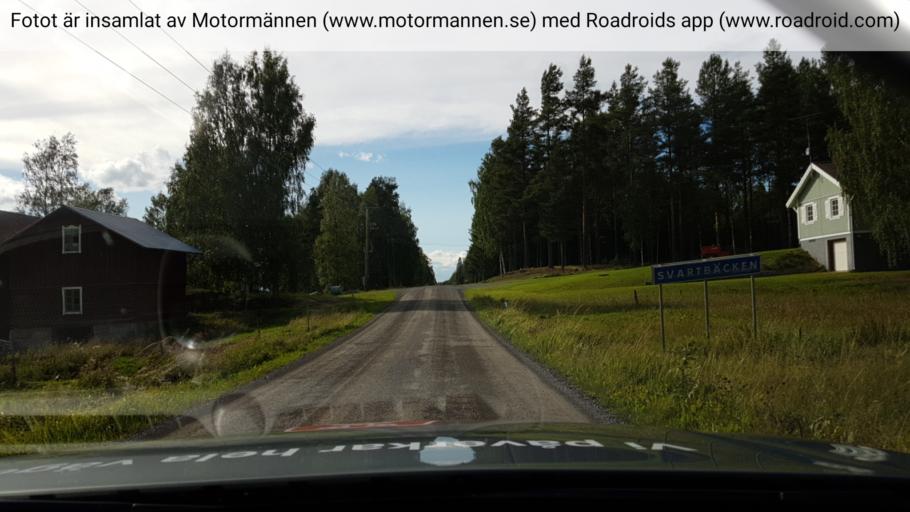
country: SE
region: Jaemtland
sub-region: Braecke Kommun
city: Braecke
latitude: 63.1955
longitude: 15.4994
